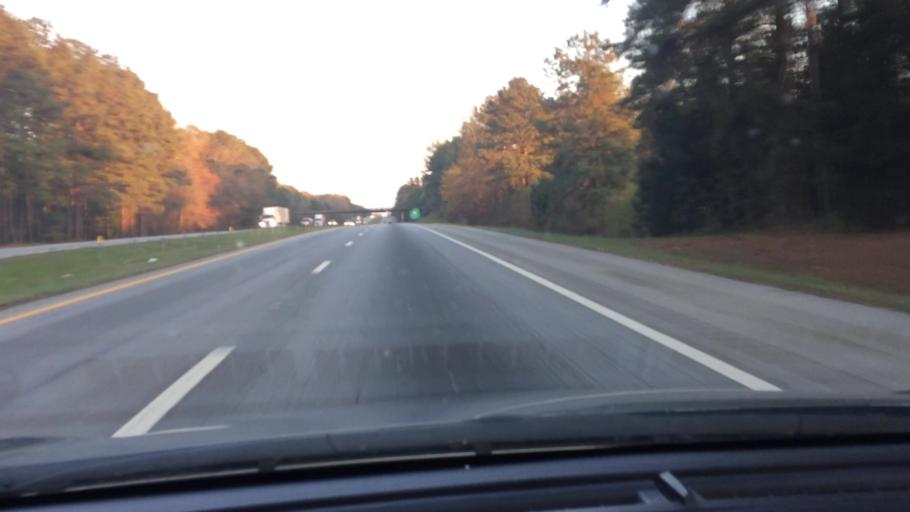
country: US
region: South Carolina
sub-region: Newberry County
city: Newberry
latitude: 34.3421
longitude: -81.6287
